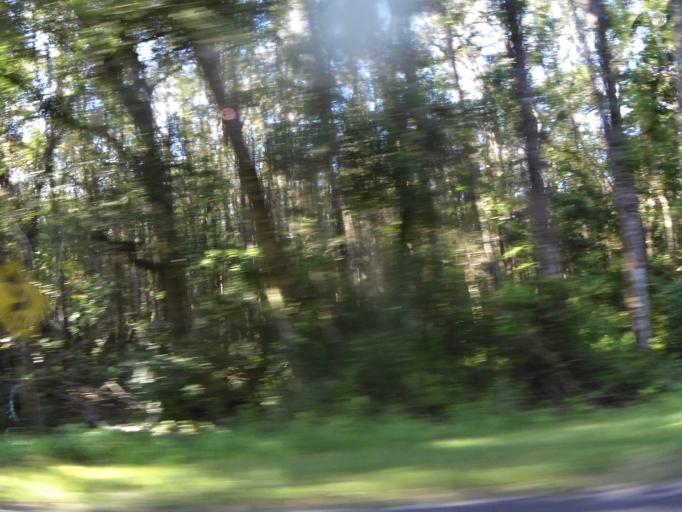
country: US
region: Florida
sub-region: Wakulla County
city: Crawfordville
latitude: 30.0690
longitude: -84.5111
